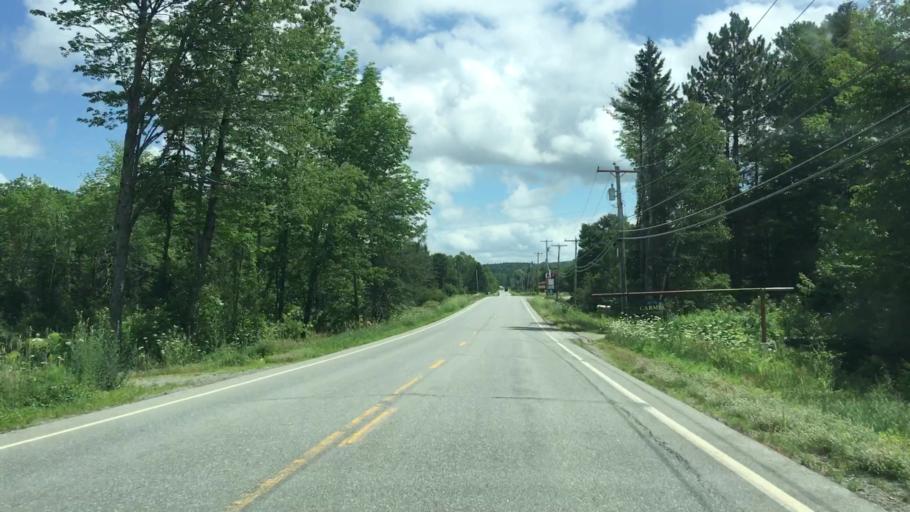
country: US
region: Maine
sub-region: Penobscot County
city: Carmel
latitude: 44.8076
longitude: -68.9910
